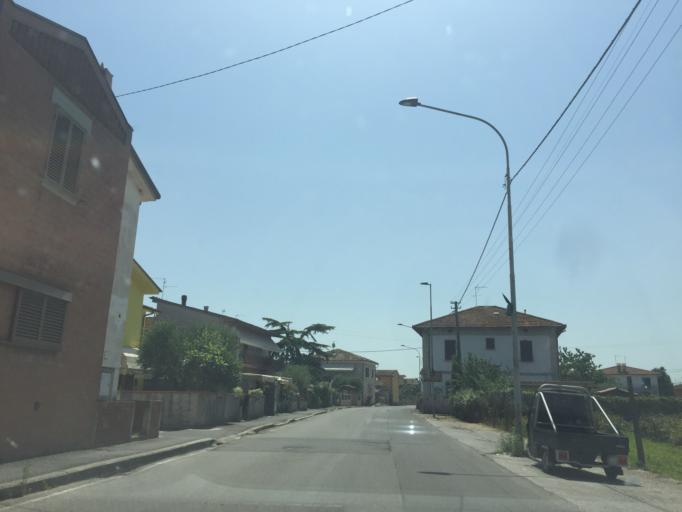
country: IT
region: Tuscany
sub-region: Provincia di Pistoia
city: Anchione
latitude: 43.8235
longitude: 10.7583
